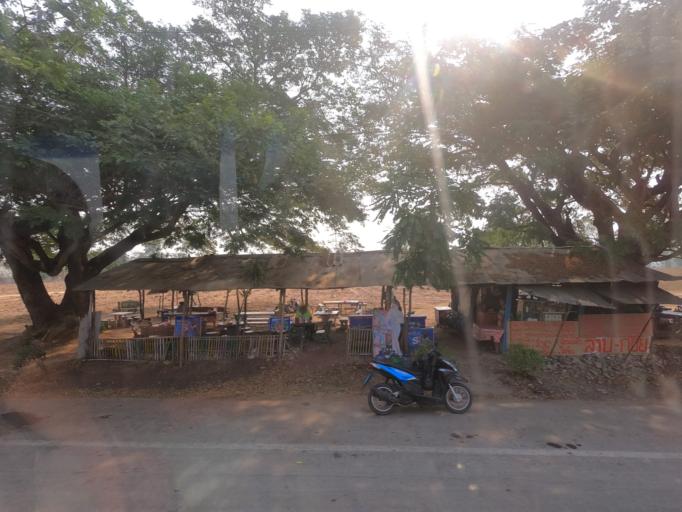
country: TH
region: Khon Kaen
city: Ban Haet
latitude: 16.2325
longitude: 102.7674
